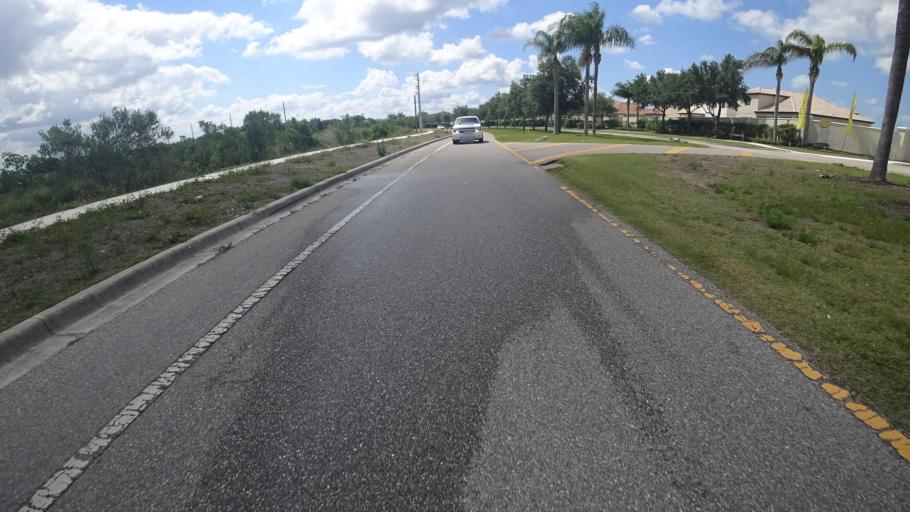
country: US
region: Florida
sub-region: Manatee County
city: Bayshore Gardens
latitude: 27.4339
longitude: -82.6201
